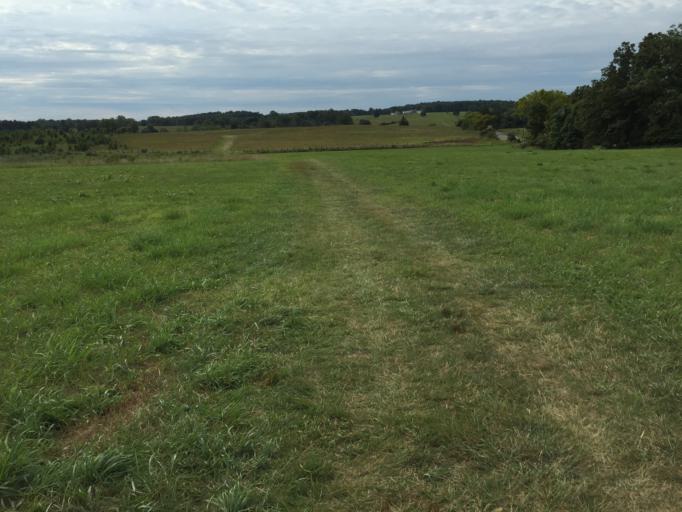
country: US
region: Virginia
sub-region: Prince William County
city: Bull Run
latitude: 38.8235
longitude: -77.5301
